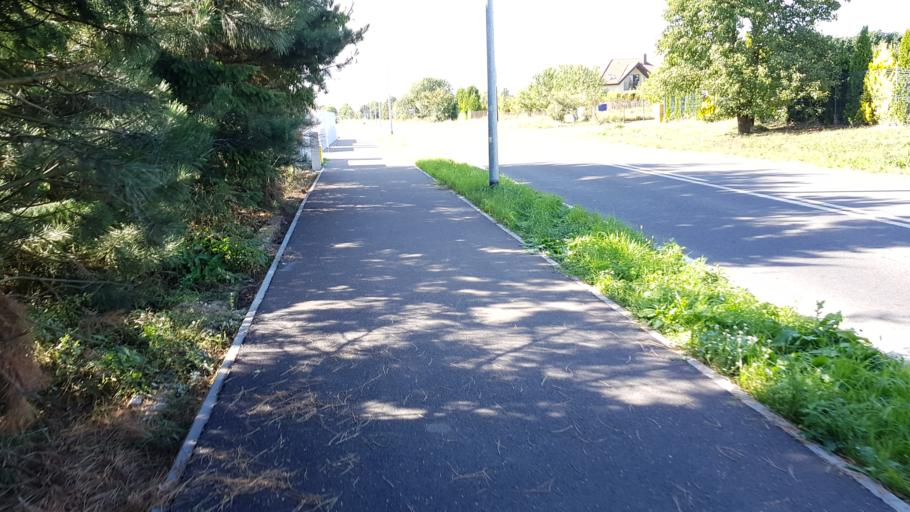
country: PL
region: West Pomeranian Voivodeship
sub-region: Powiat policki
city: Przeclaw
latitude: 53.3521
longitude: 14.4716
